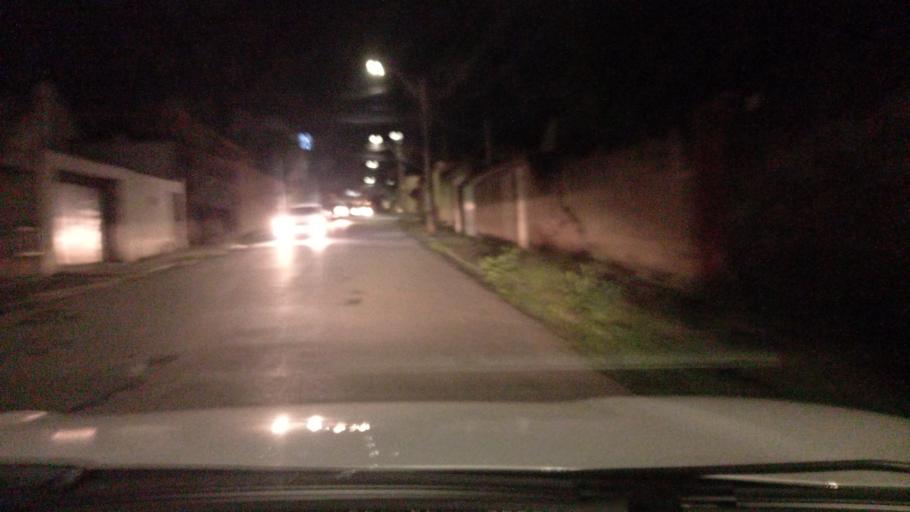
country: BR
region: Minas Gerais
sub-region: Belo Horizonte
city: Belo Horizonte
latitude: -19.8970
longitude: -43.9575
